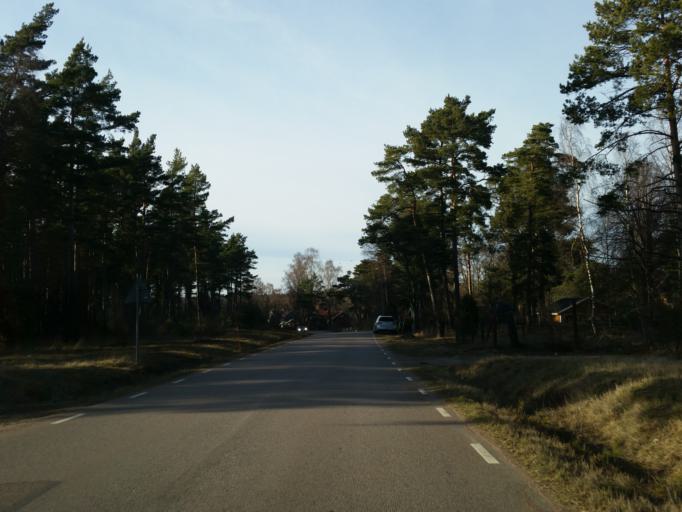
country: SE
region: Kalmar
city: Faerjestaden
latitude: 56.7797
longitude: 16.4510
